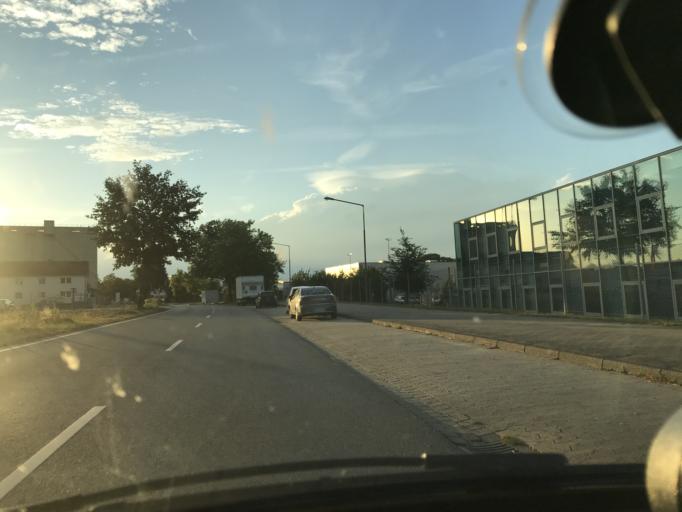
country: DE
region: Lower Saxony
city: Buxtehude
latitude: 53.4634
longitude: 9.7147
